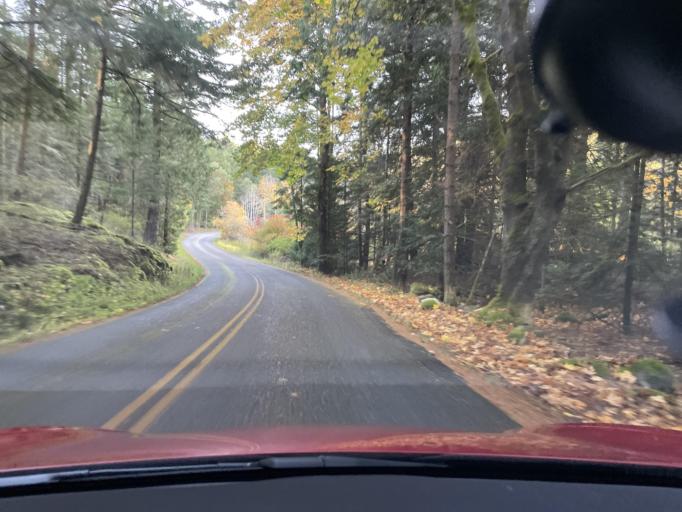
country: US
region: Washington
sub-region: San Juan County
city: Friday Harbor
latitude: 48.5218
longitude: -123.1446
